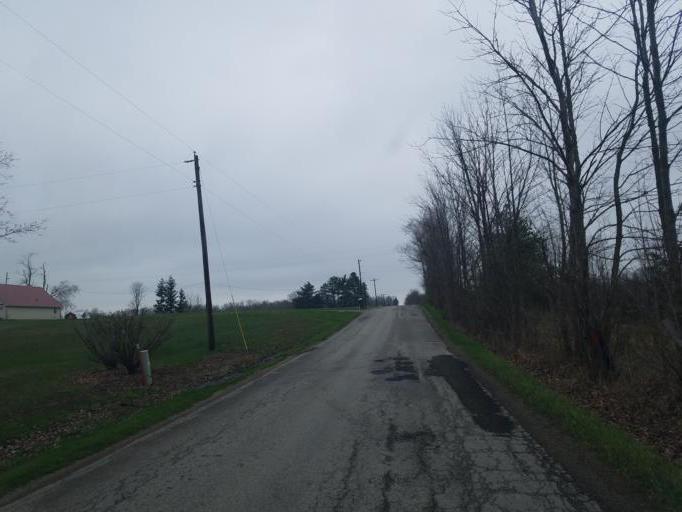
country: US
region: Ohio
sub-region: Morrow County
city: Mount Gilead
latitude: 40.5688
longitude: -82.8056
